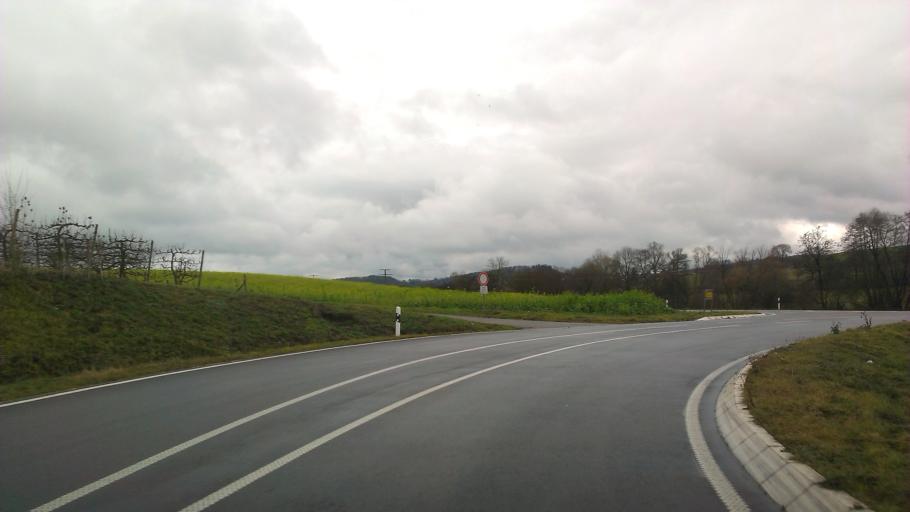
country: DE
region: Baden-Wuerttemberg
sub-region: Karlsruhe Region
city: Kurnbach
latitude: 49.0772
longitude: 8.8276
